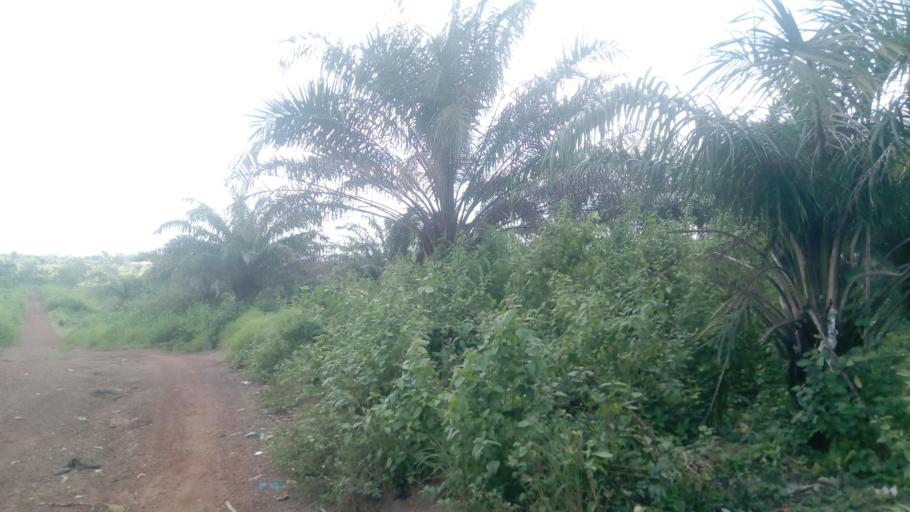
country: SL
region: Northern Province
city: Makeni
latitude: 8.9307
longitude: -12.0490
